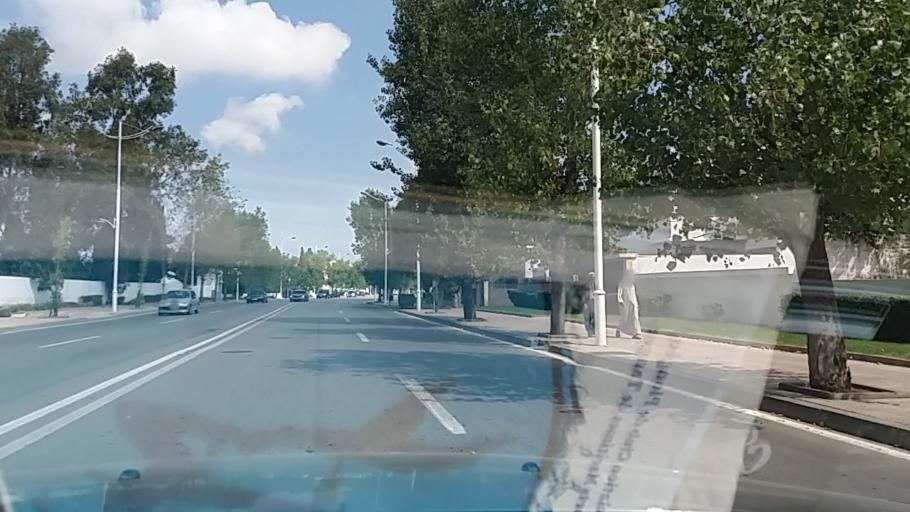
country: MA
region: Tanger-Tetouan
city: Tetouan
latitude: 35.5787
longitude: -5.3388
